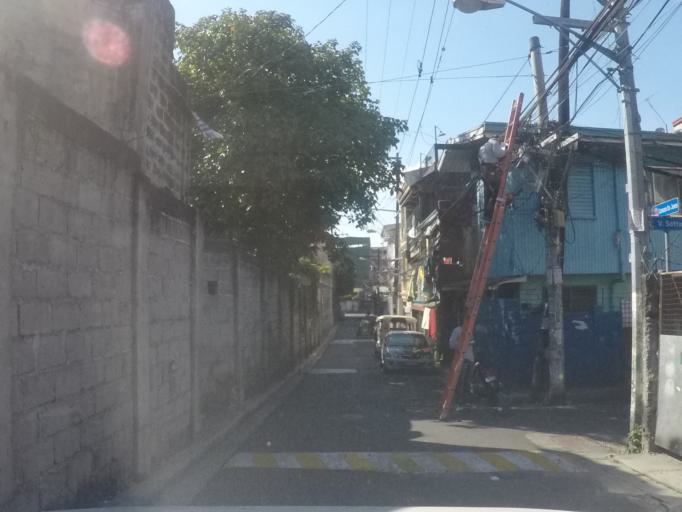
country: PH
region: Metro Manila
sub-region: San Juan
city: San Juan
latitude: 14.6078
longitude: 121.0291
